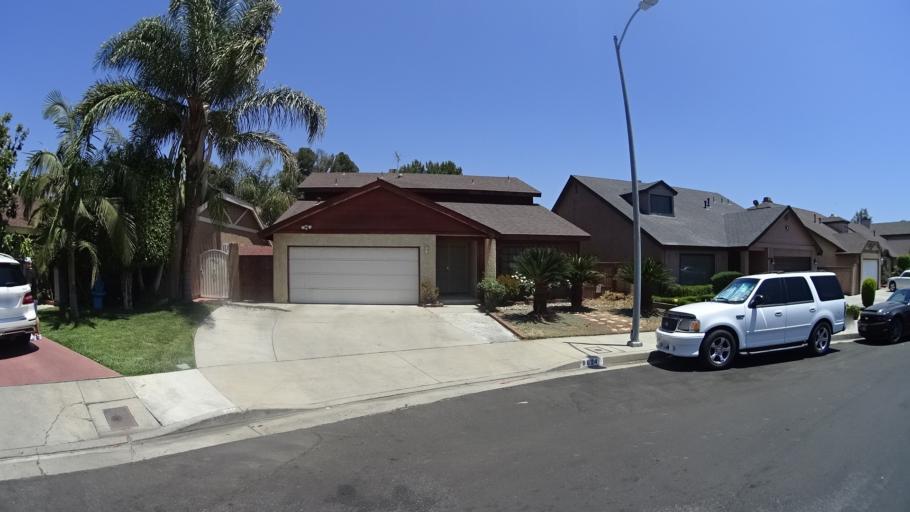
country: US
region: California
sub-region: Los Angeles County
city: Van Nuys
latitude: 34.2271
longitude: -118.4602
